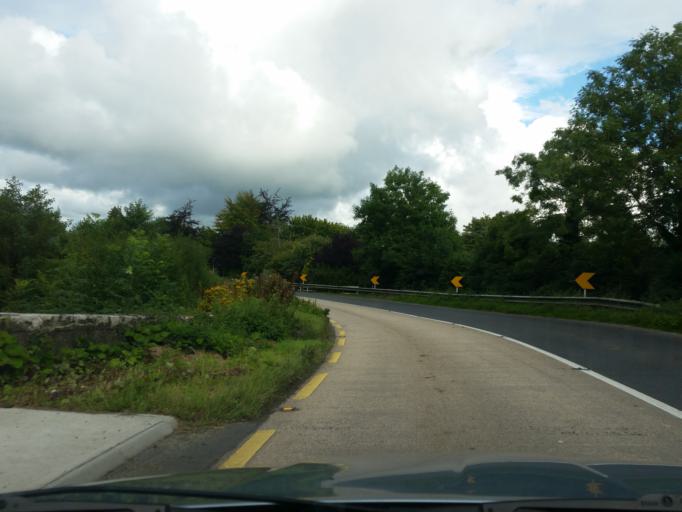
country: IE
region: Ulster
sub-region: An Cabhan
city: Belturbet
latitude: 54.1143
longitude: -7.3482
